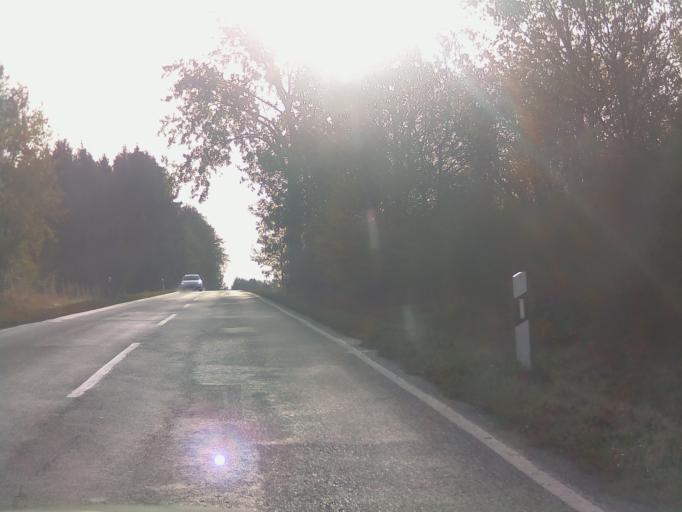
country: DE
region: Hesse
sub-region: Regierungsbezirk Kassel
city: Hosenfeld
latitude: 50.5087
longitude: 9.4875
